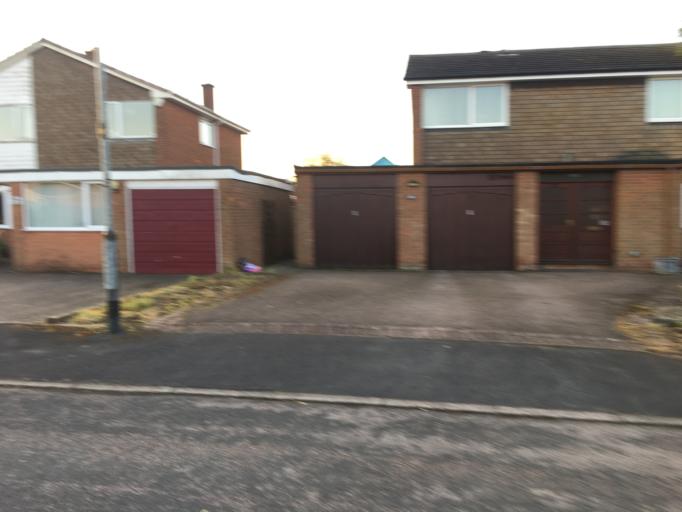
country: GB
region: England
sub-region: Leicestershire
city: Houghton on the Hill
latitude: 52.6244
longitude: -0.9929
